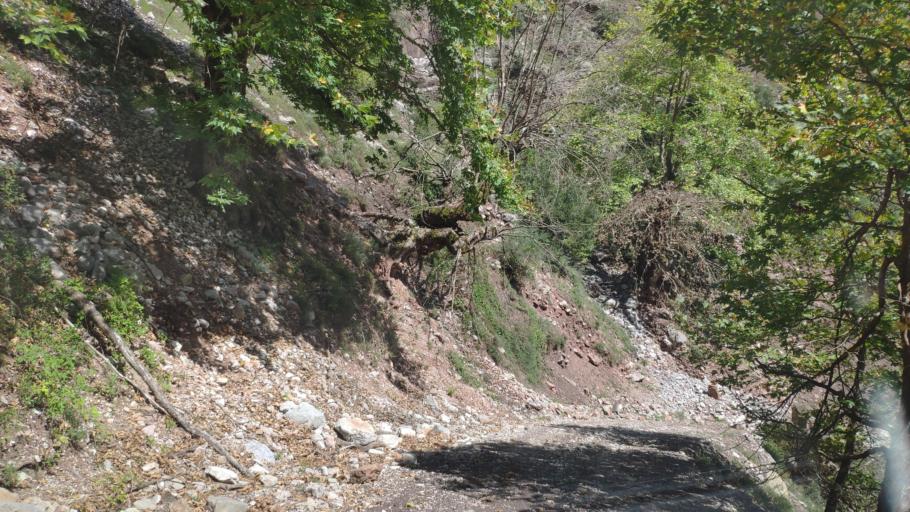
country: GR
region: Central Greece
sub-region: Nomos Evrytanias
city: Kerasochori
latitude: 39.1251
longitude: 21.6546
